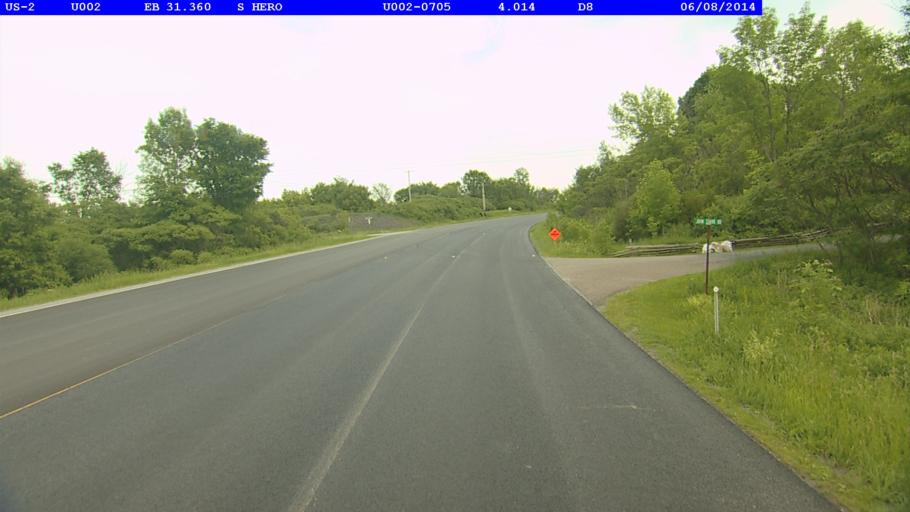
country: US
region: New York
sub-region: Clinton County
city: Cumberland Head
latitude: 44.6463
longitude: -73.2840
